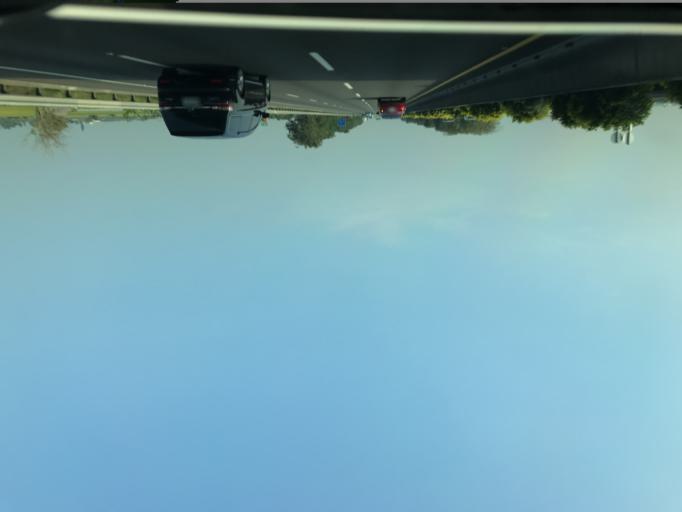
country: TW
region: Taiwan
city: Xinying
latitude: 23.3523
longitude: 120.3297
